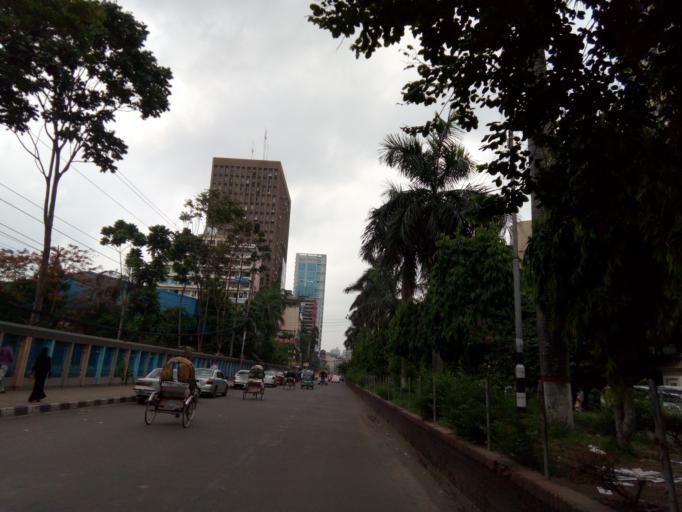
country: BD
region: Dhaka
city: Paltan
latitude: 23.7263
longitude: 90.4151
